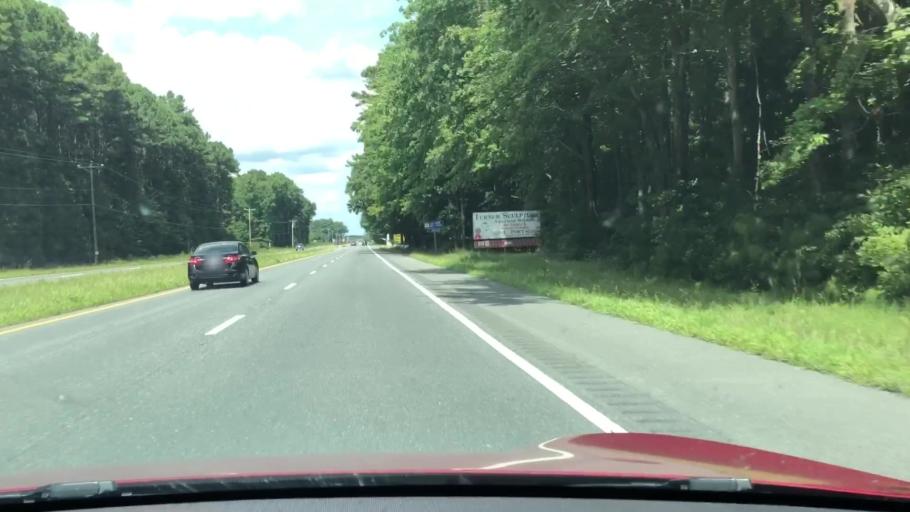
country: US
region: Virginia
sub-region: Northampton County
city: Cape Charles
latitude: 37.2565
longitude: -75.9734
